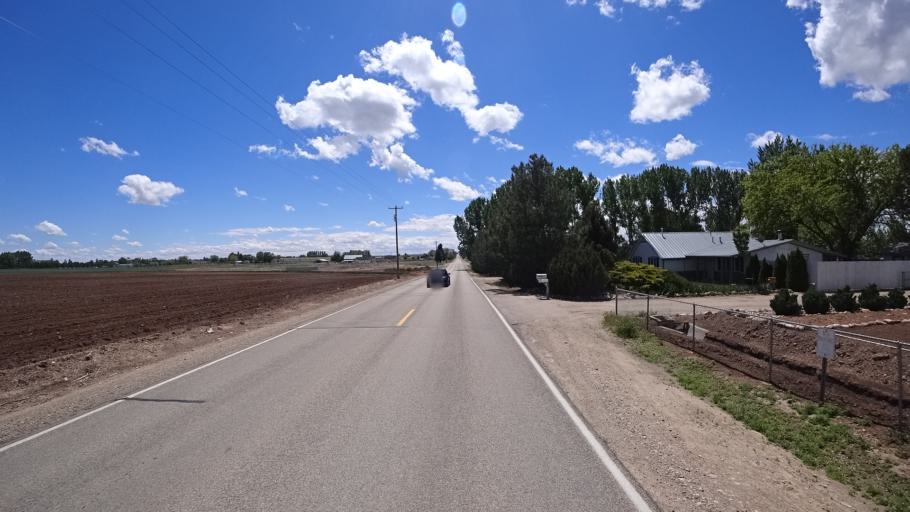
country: US
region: Idaho
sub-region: Ada County
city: Meridian
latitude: 43.5816
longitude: -116.4537
